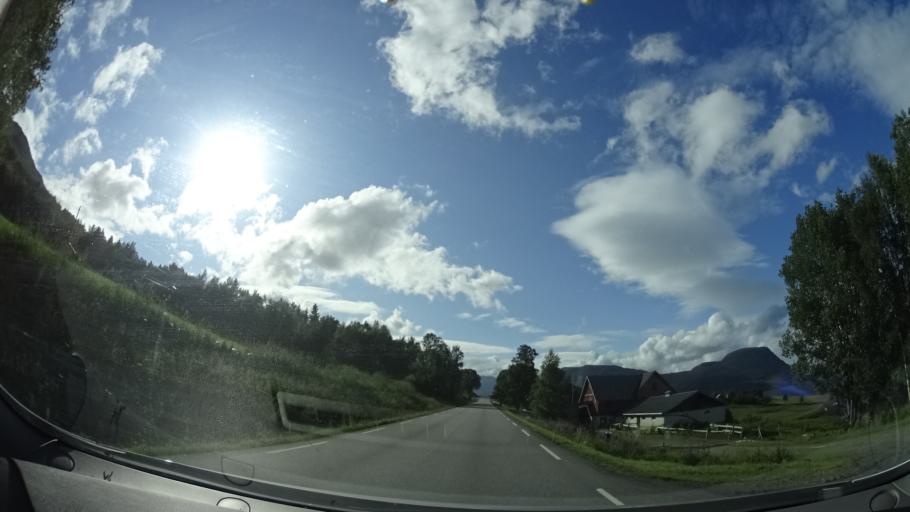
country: NO
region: More og Romsdal
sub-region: Halsa
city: Liaboen
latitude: 63.1340
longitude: 8.4571
